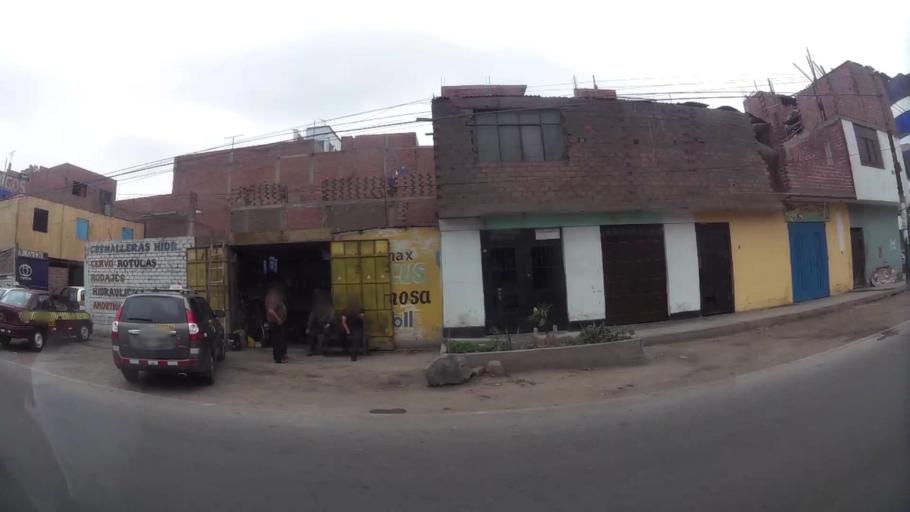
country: PE
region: Lima
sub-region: Lima
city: Independencia
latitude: -11.9728
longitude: -77.0816
